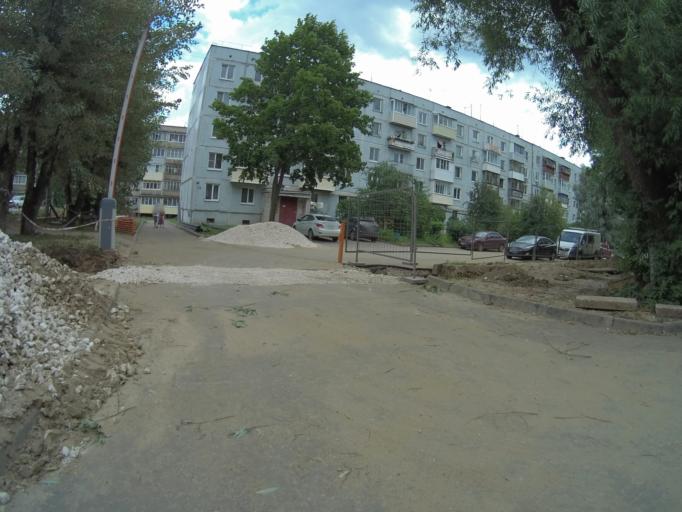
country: RU
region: Vladimir
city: Vladimir
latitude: 56.1337
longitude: 40.3713
